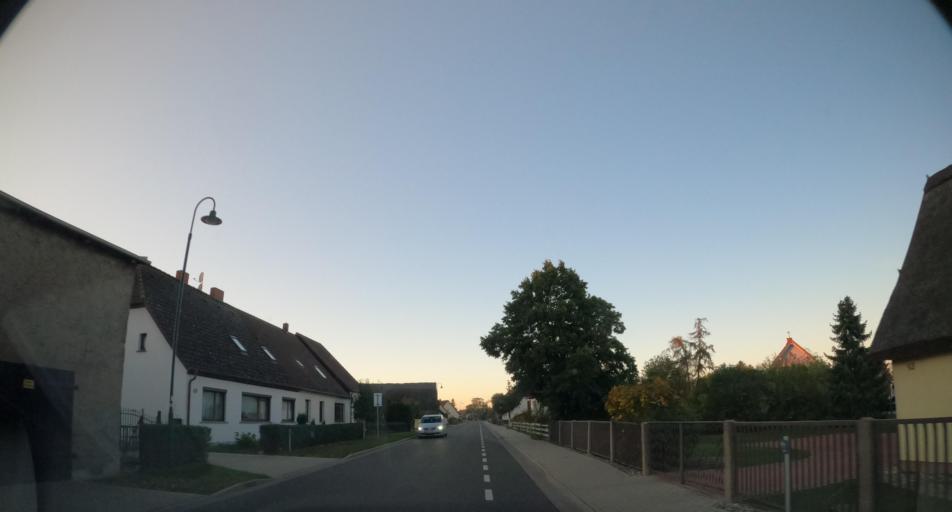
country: DE
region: Mecklenburg-Vorpommern
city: Ueckermunde
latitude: 53.7548
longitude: 14.0169
